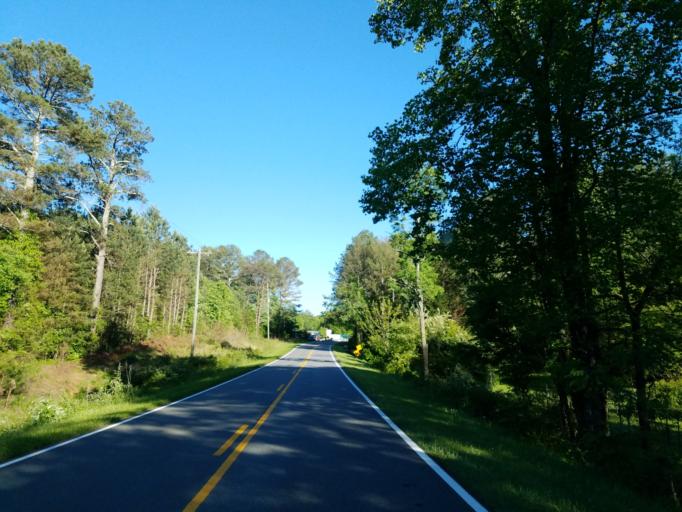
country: US
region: Georgia
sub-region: Gilmer County
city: Ellijay
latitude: 34.6760
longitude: -84.3708
